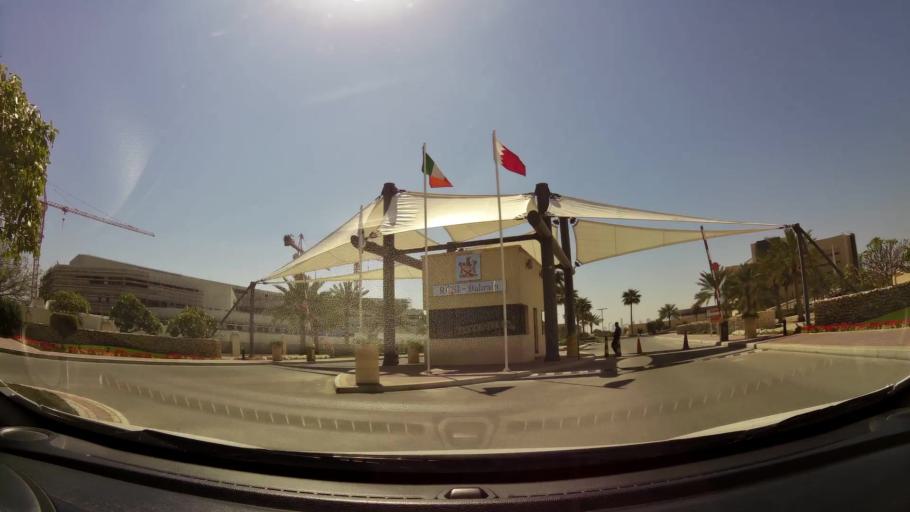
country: BH
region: Muharraq
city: Al Muharraq
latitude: 26.2636
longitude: 50.5980
